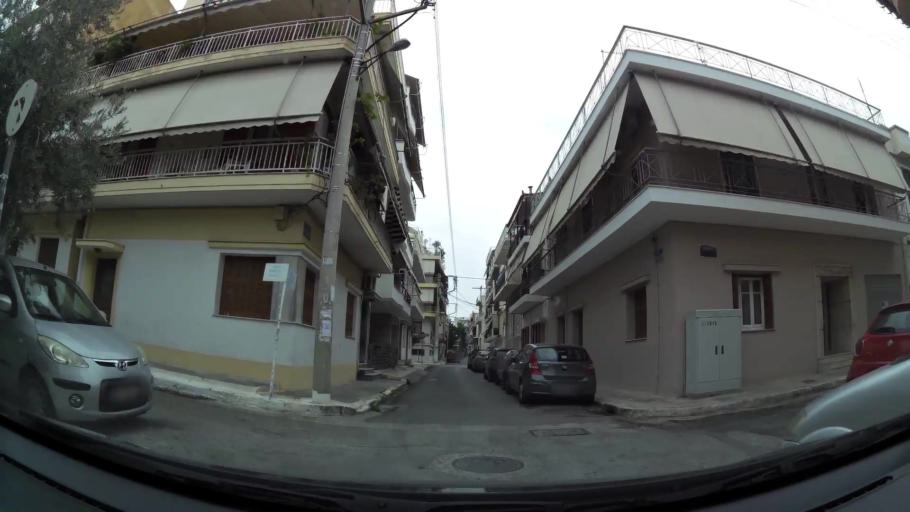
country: GR
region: Attica
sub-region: Nomos Piraios
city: Agios Ioannis Rentis
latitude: 37.9562
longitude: 23.6572
